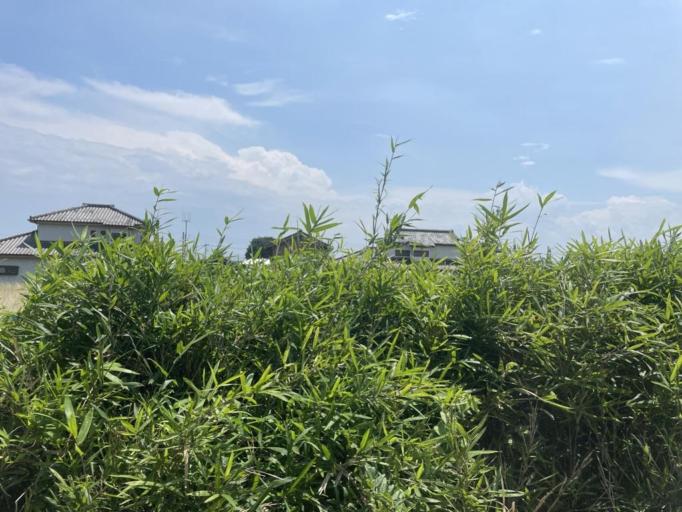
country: JP
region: Gunma
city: Omamacho-omama
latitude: 36.4148
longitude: 139.1779
